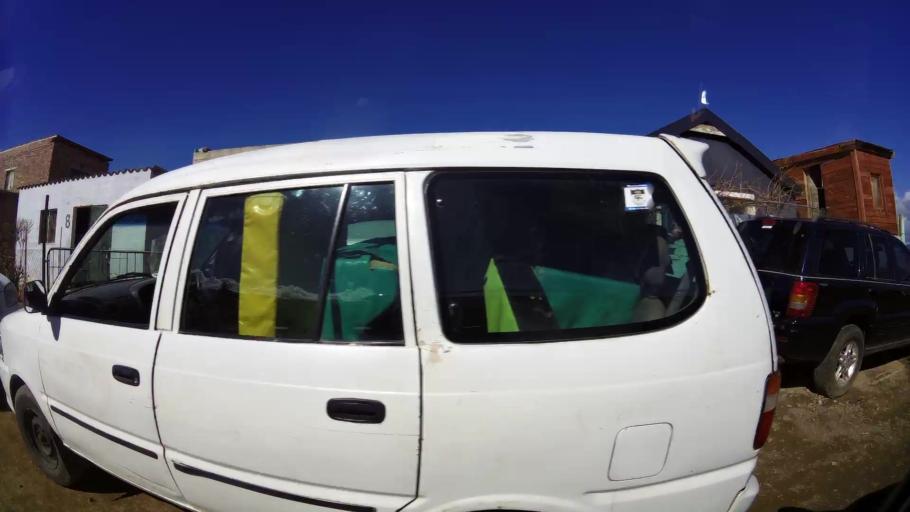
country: ZA
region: Western Cape
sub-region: Cape Winelands District Municipality
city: Ashton
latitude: -33.7929
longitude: 19.8810
